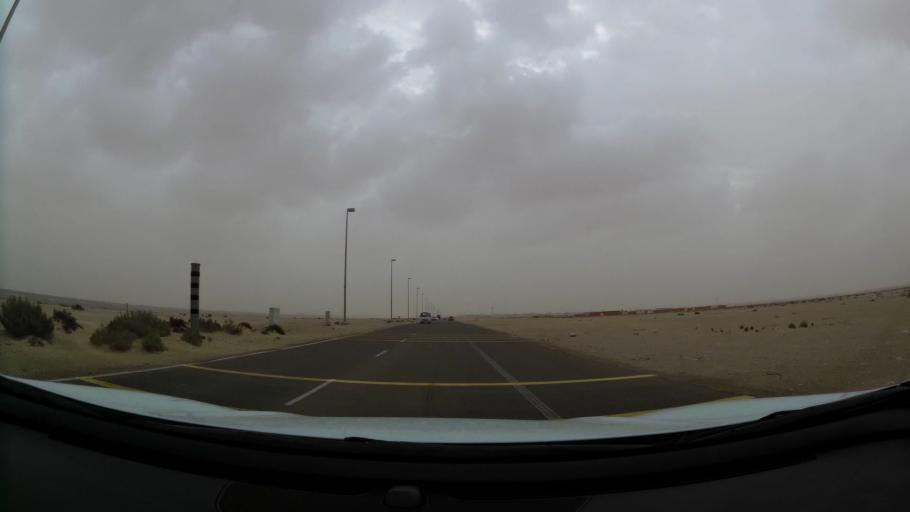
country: AE
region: Abu Dhabi
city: Abu Dhabi
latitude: 24.4612
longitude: 54.6983
